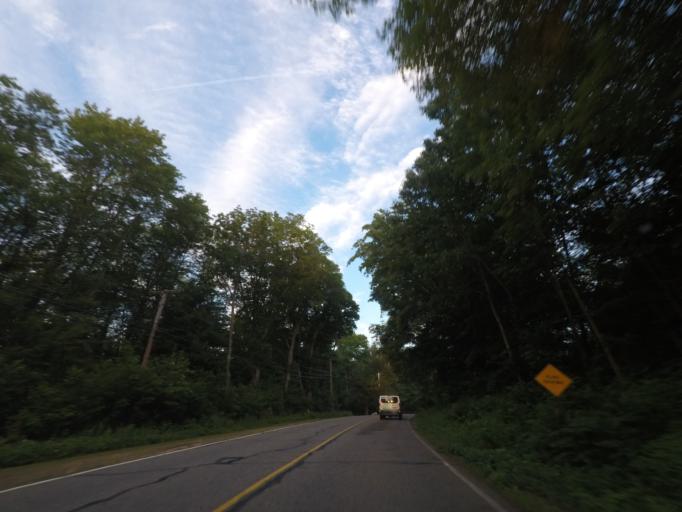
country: US
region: Massachusetts
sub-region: Worcester County
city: Warren
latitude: 42.1890
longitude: -72.1741
